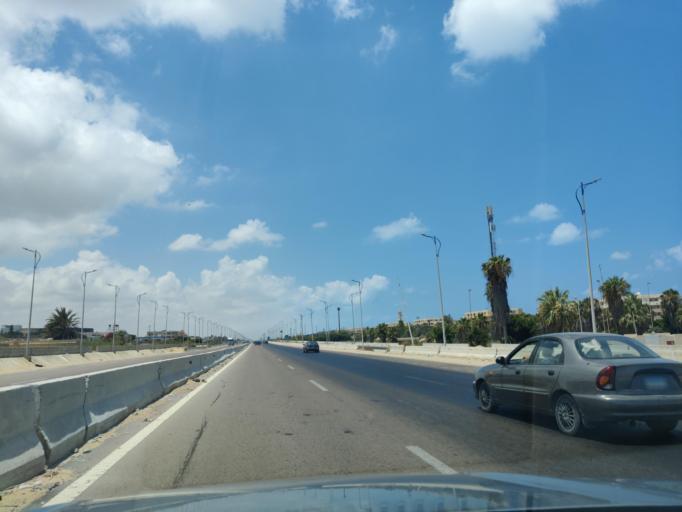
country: EG
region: Muhafazat Matruh
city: Al `Alamayn
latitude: 30.9355
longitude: 29.4886
